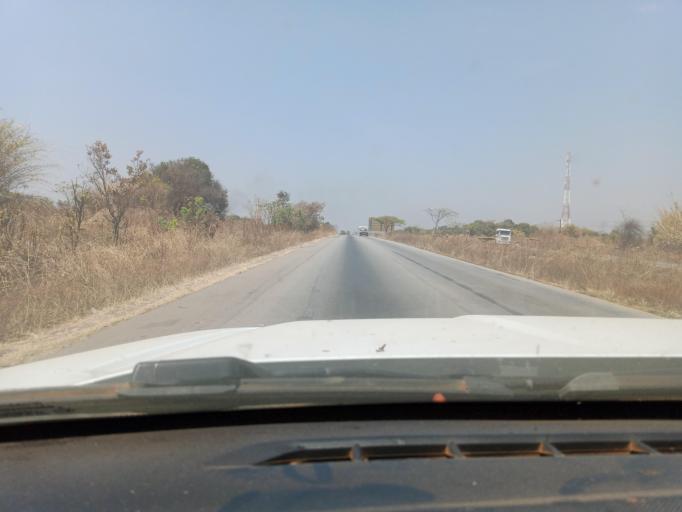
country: ZM
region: Copperbelt
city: Luanshya
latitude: -12.9949
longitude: 28.4191
